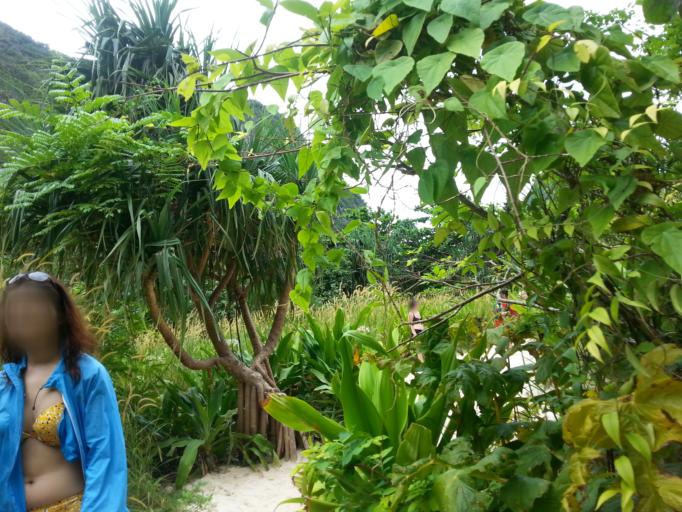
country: TH
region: Krabi
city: Saladan
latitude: 7.6761
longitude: 98.7662
